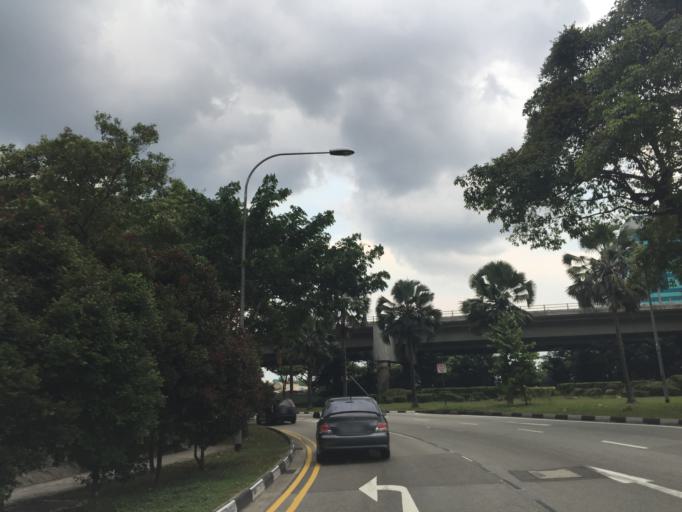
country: MY
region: Johor
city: Johor Bahru
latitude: 1.3236
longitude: 103.6966
